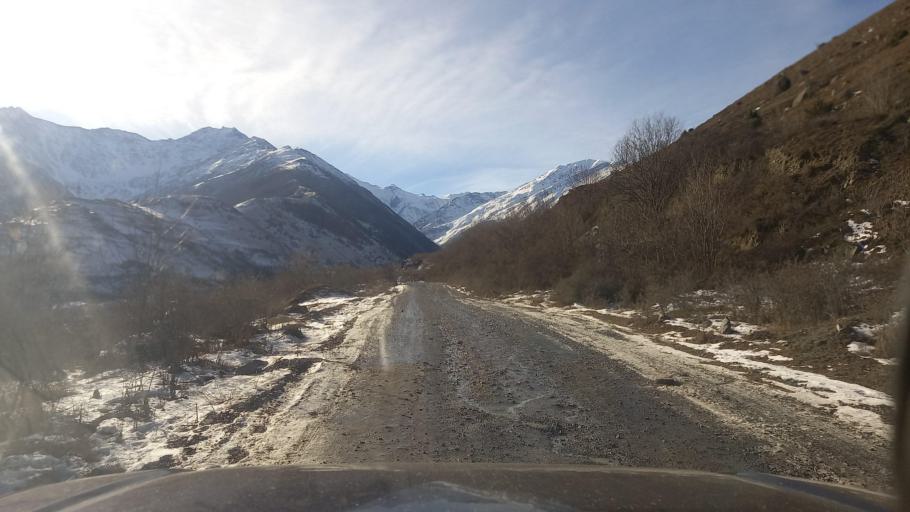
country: RU
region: Ingushetiya
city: Dzhayrakh
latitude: 42.8522
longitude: 44.5201
